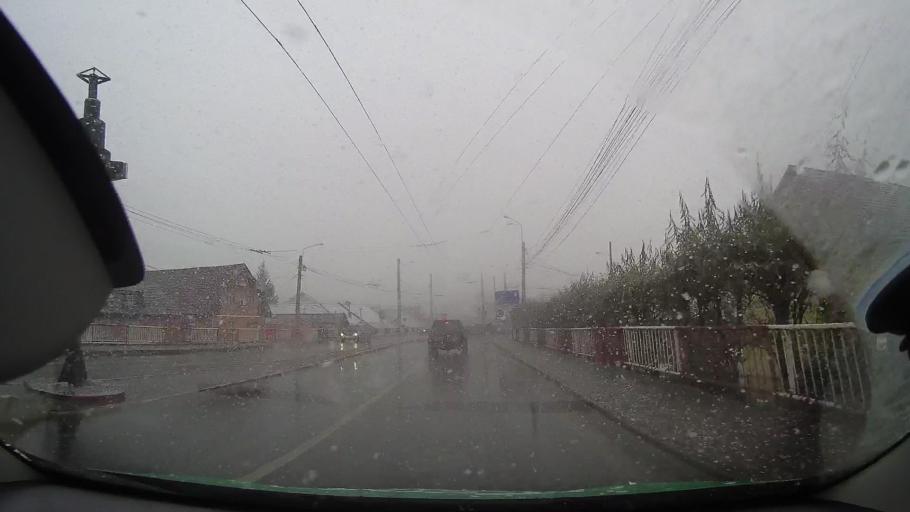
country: RO
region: Sibiu
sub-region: Municipiul Medias
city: Medias
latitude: 46.1706
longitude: 24.3469
